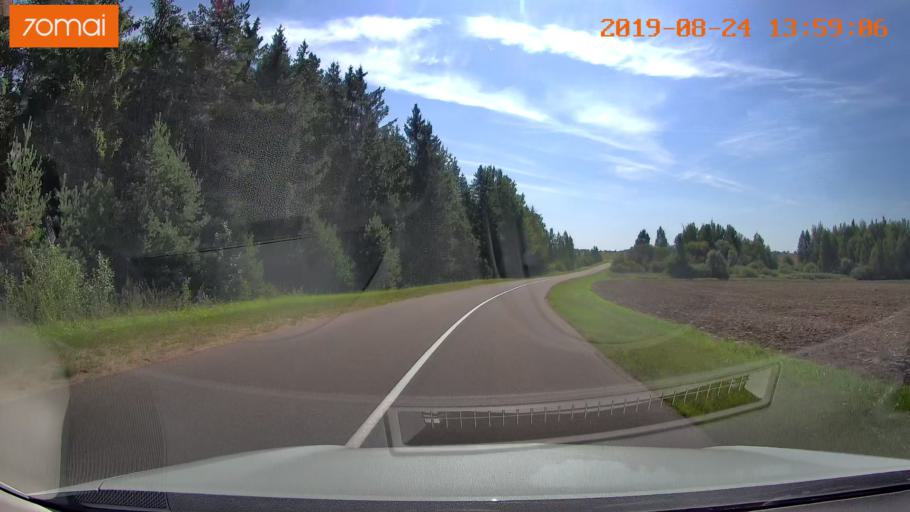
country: BY
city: Michanovichi
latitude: 53.6025
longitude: 27.6790
